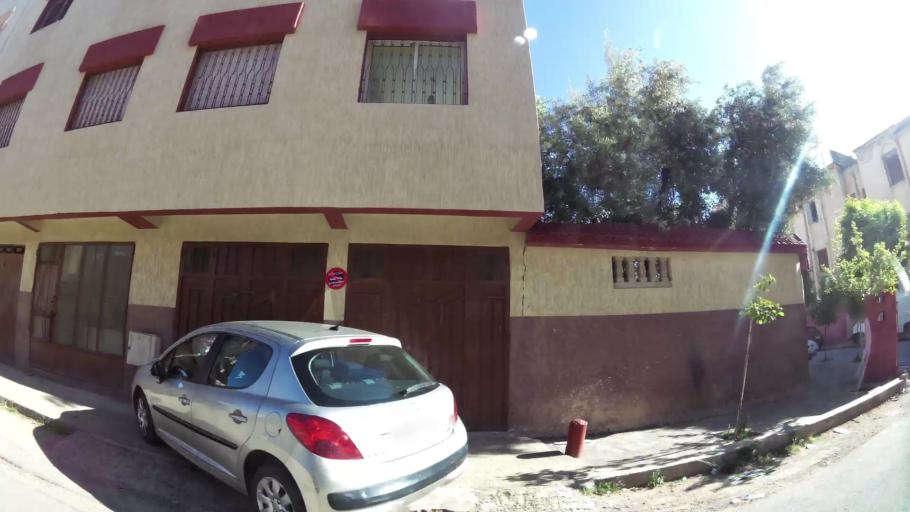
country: MA
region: Meknes-Tafilalet
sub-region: Meknes
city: Meknes
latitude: 33.8892
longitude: -5.5028
